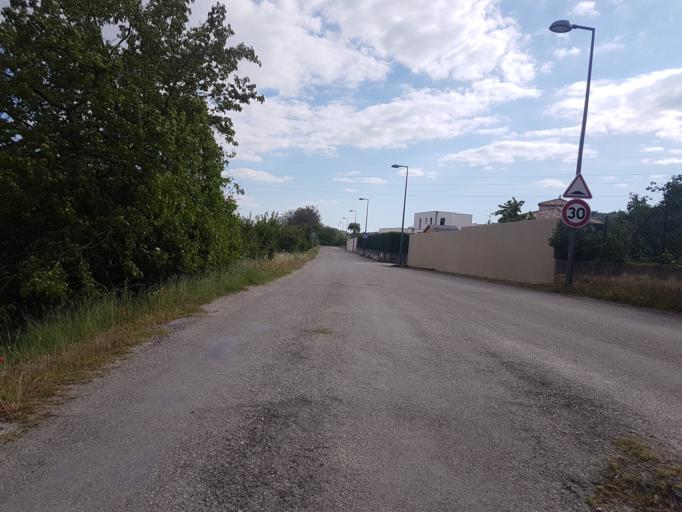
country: FR
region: Rhone-Alpes
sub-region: Departement de l'Ardeche
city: Guilherand-Granges
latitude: 44.9190
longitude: 4.8657
